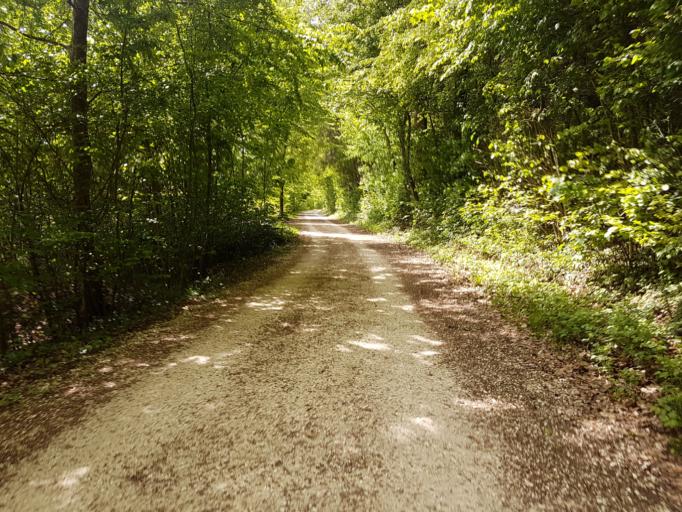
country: CH
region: Aargau
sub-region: Bezirk Brugg
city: Rupperswil
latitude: 47.4127
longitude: 8.1116
